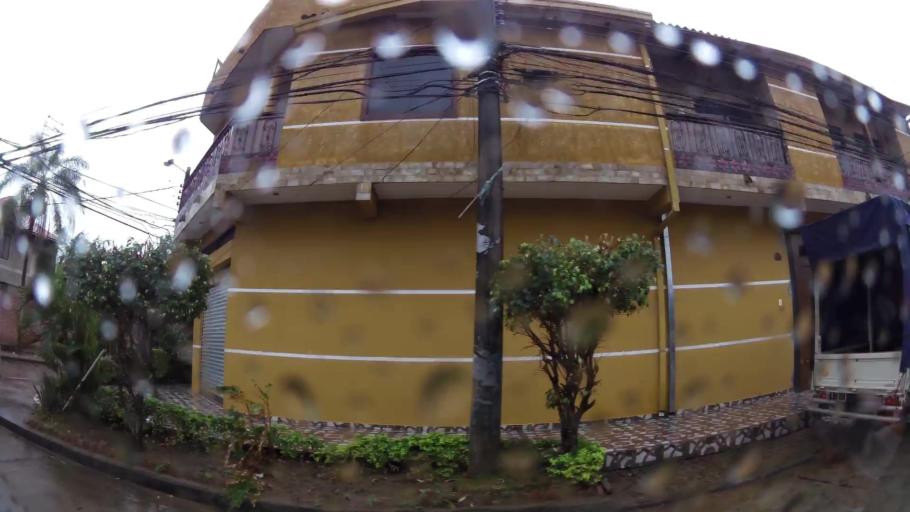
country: BO
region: Santa Cruz
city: Santa Cruz de la Sierra
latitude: -17.7878
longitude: -63.2140
